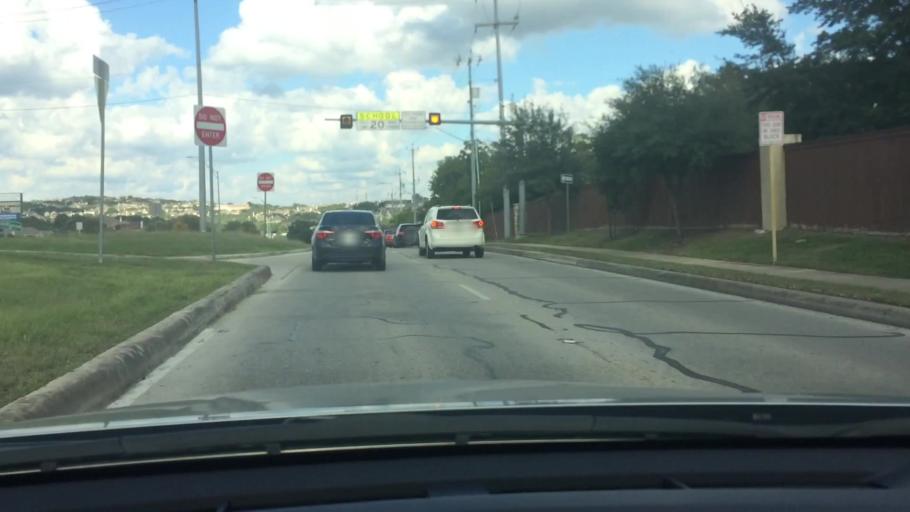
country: US
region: Texas
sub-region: Bexar County
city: Hollywood Park
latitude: 29.6401
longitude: -98.4415
